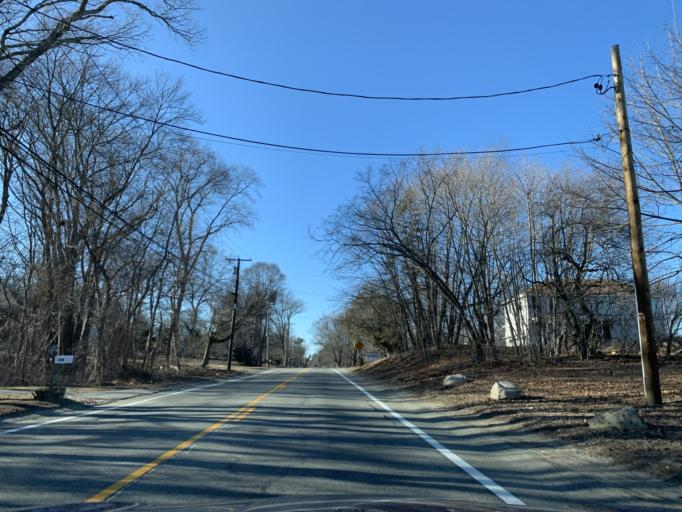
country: US
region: Rhode Island
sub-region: Providence County
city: North Providence
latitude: 41.8835
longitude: -71.4802
